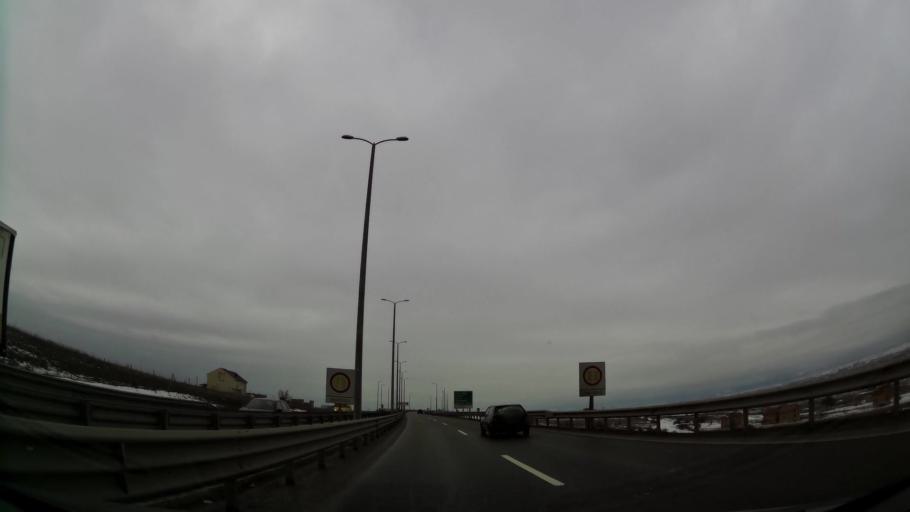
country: XK
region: Pristina
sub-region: Komuna e Prishtines
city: Pristina
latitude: 42.6305
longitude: 21.1365
